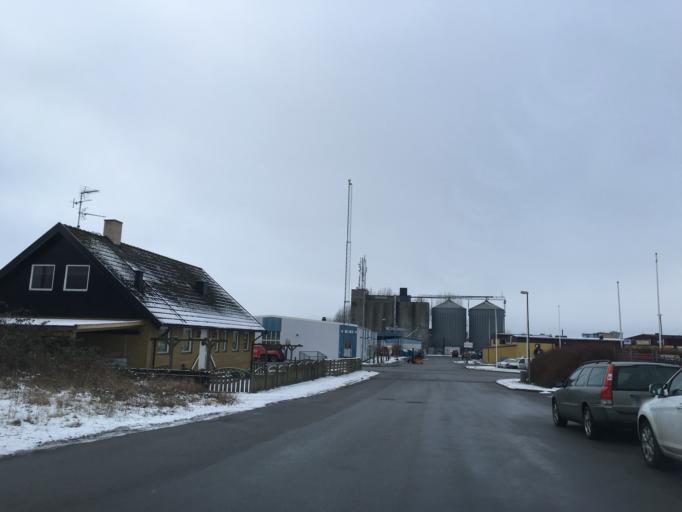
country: SE
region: Skane
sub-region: Vellinge Kommun
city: Vellinge
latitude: 55.4747
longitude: 13.0242
